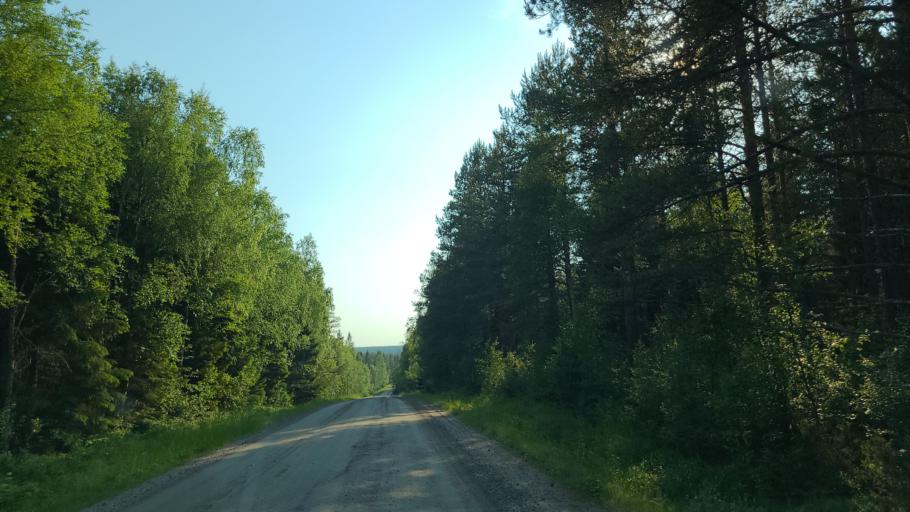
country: SE
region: Vaesterbotten
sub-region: Skelleftea Kommun
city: Burea
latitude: 64.3614
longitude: 21.4320
